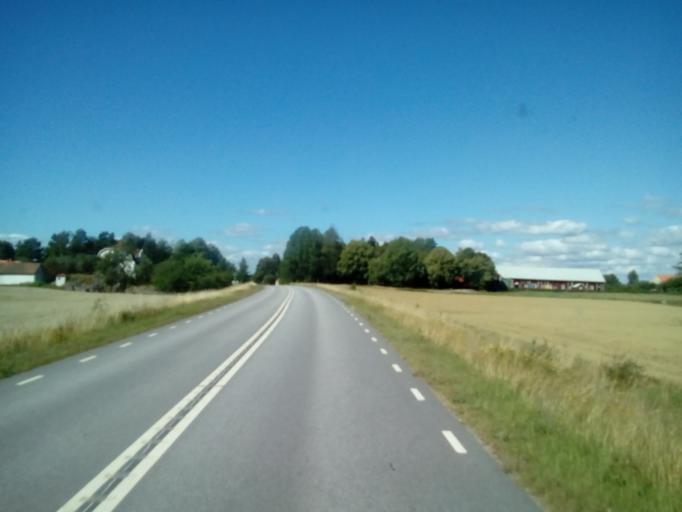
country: SE
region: Kalmar
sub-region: Vimmerby Kommun
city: Sodra Vi
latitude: 57.9223
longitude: 15.9379
